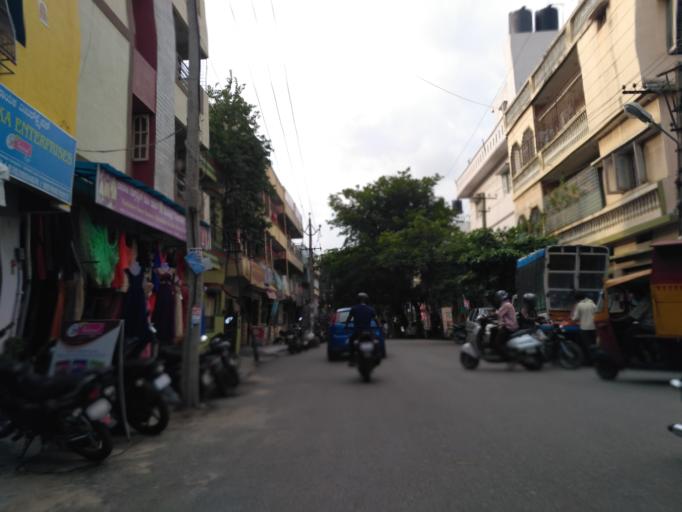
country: IN
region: Karnataka
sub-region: Bangalore Urban
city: Bangalore
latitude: 12.9771
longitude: 77.5388
